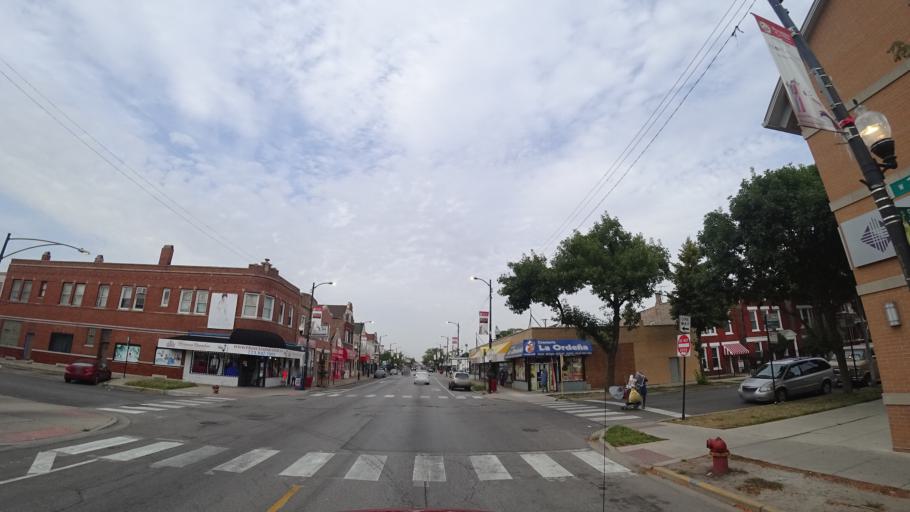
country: US
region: Illinois
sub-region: Cook County
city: Cicero
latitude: 41.8446
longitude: -87.7060
